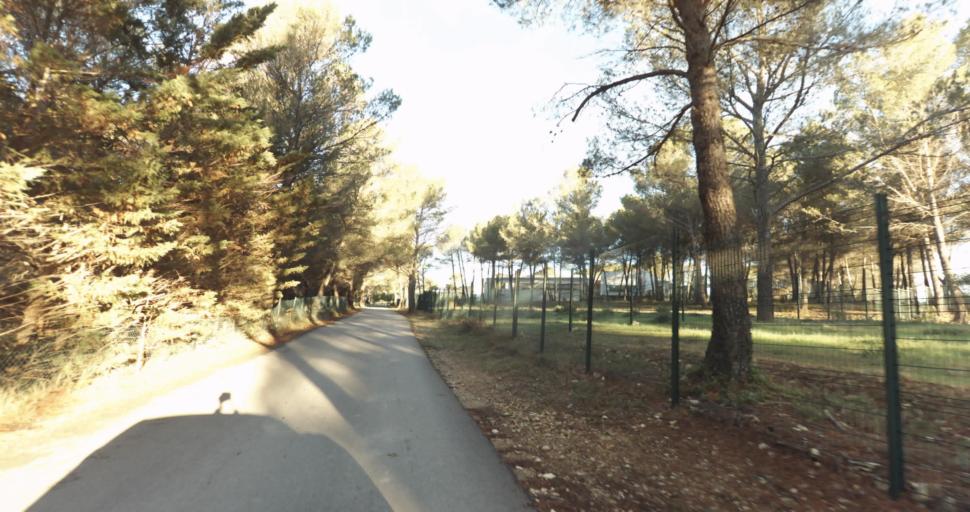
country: FR
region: Provence-Alpes-Cote d'Azur
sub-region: Departement des Bouches-du-Rhone
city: Venelles
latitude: 43.5932
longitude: 5.4960
